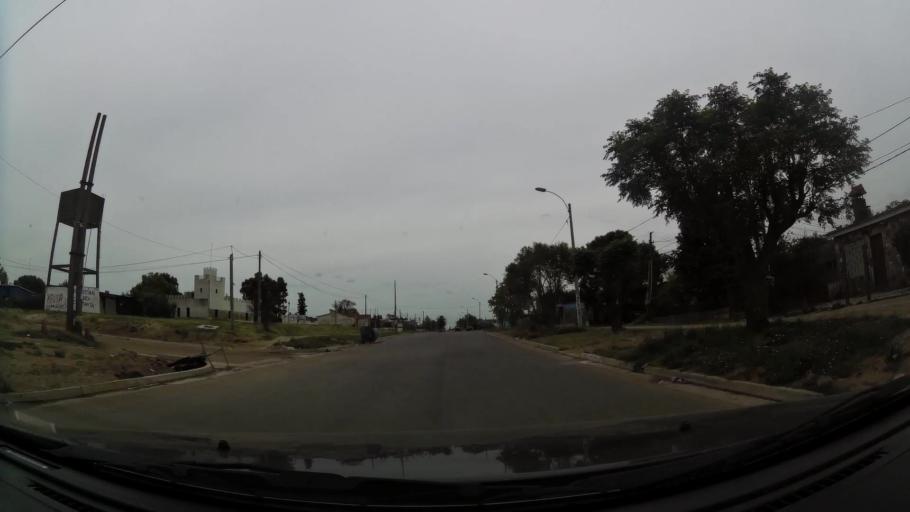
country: UY
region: Canelones
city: Las Piedras
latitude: -34.7435
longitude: -56.2157
